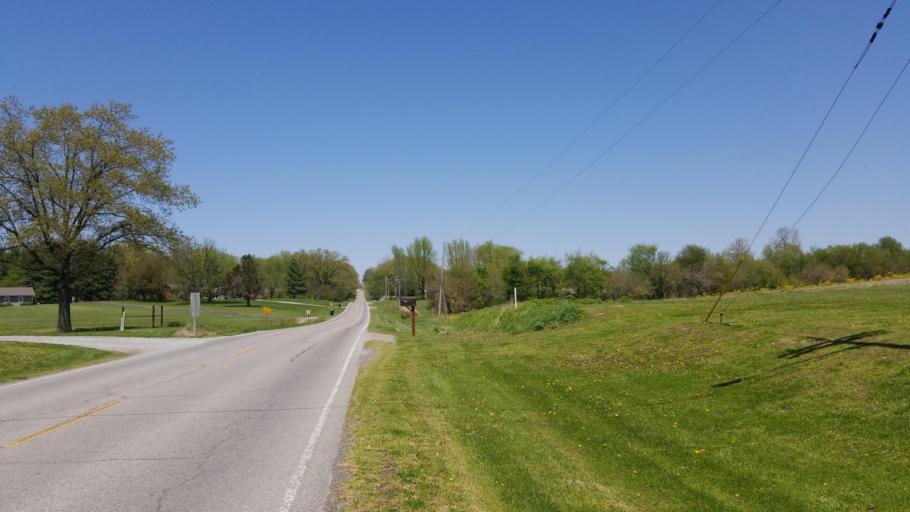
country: US
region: Illinois
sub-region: Saline County
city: Harrisburg
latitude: 37.8441
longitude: -88.6053
